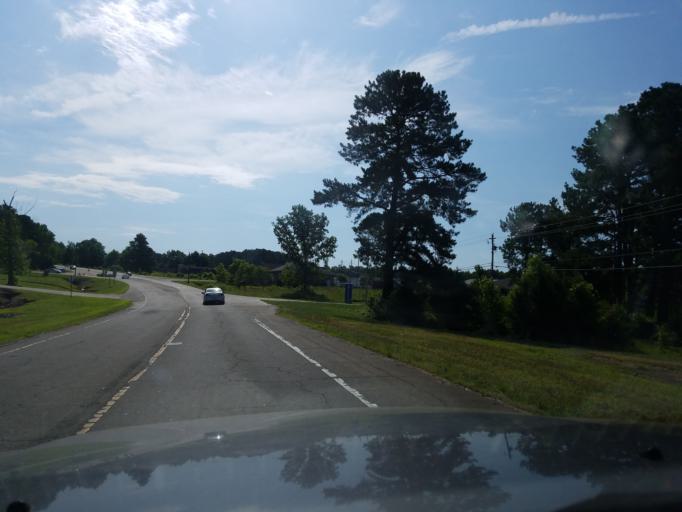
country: US
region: North Carolina
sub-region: Granville County
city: Oxford
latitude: 36.3130
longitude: -78.5552
